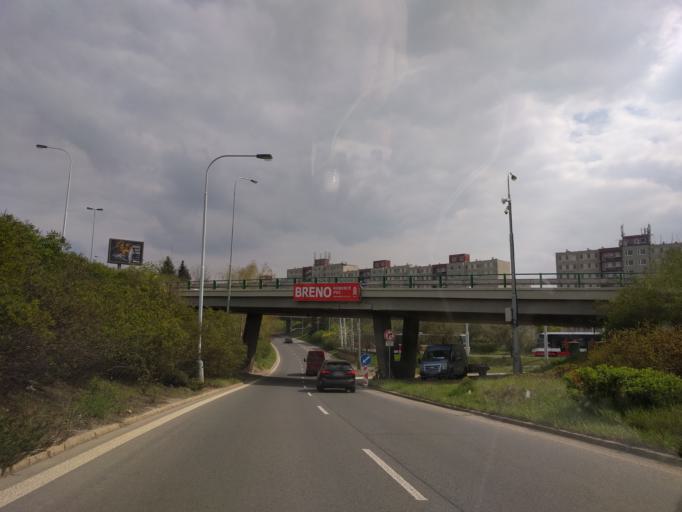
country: CZ
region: Praha
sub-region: Praha 14
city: Hostavice
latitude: 50.1080
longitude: 14.5480
